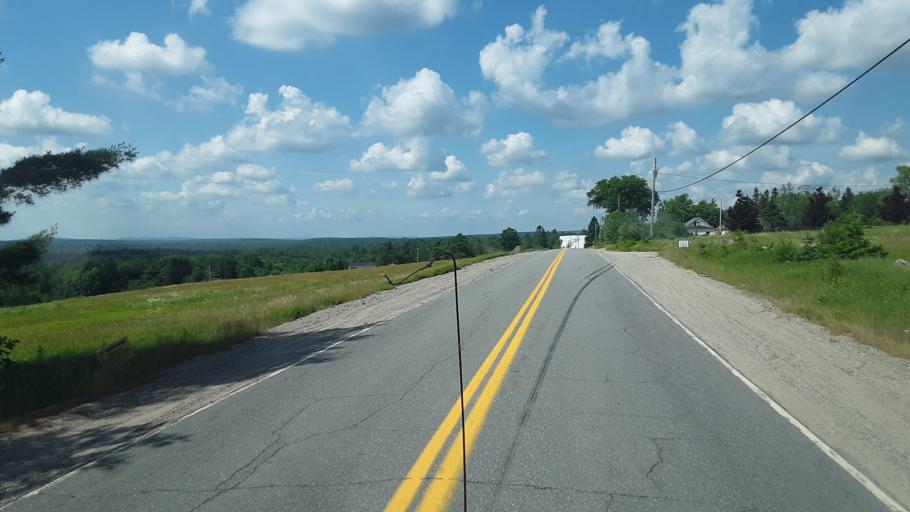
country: US
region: Maine
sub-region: Washington County
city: Machias
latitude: 44.9483
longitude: -67.6639
